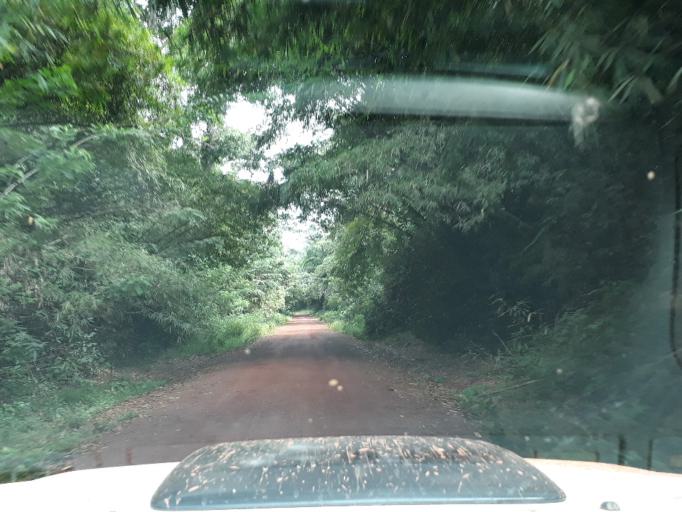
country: CD
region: Eastern Province
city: Buta
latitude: 2.2888
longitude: 25.0534
